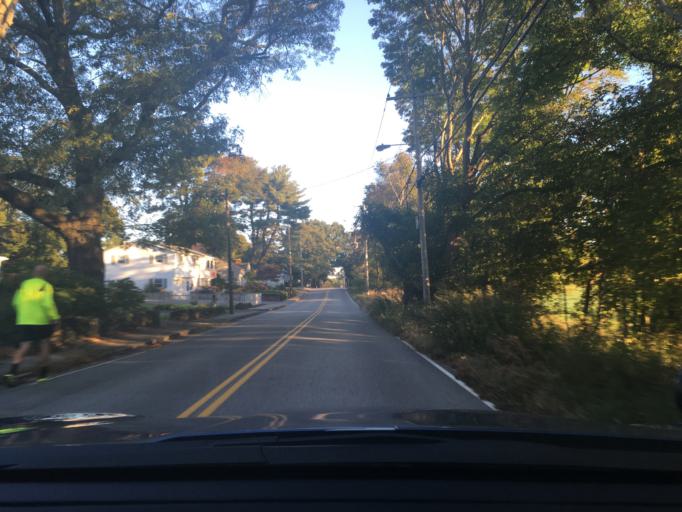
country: US
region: Rhode Island
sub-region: Kent County
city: East Greenwich
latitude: 41.6409
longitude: -71.4550
